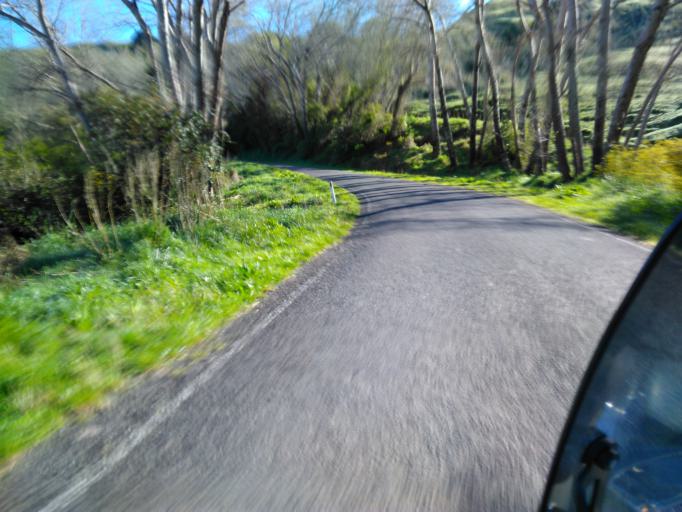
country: NZ
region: Gisborne
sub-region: Gisborne District
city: Gisborne
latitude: -38.4340
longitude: 177.7432
